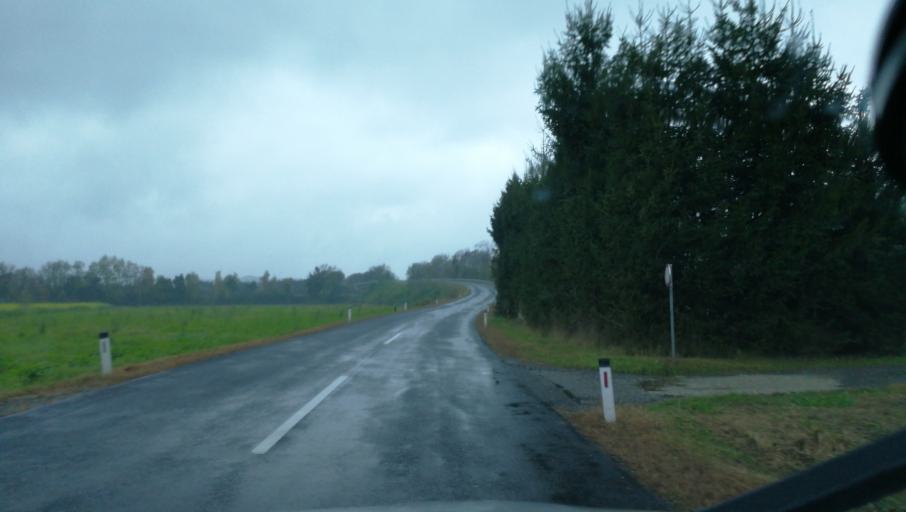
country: AT
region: Styria
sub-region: Politischer Bezirk Leibnitz
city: Sankt Veit am Vogau
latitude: 46.7433
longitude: 15.6205
